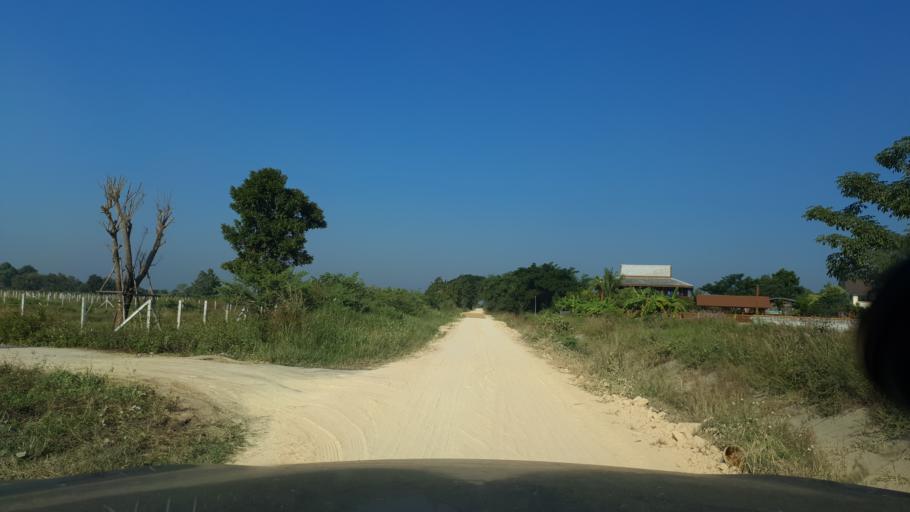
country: TH
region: Chiang Mai
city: San Kamphaeng
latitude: 18.7042
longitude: 99.1319
